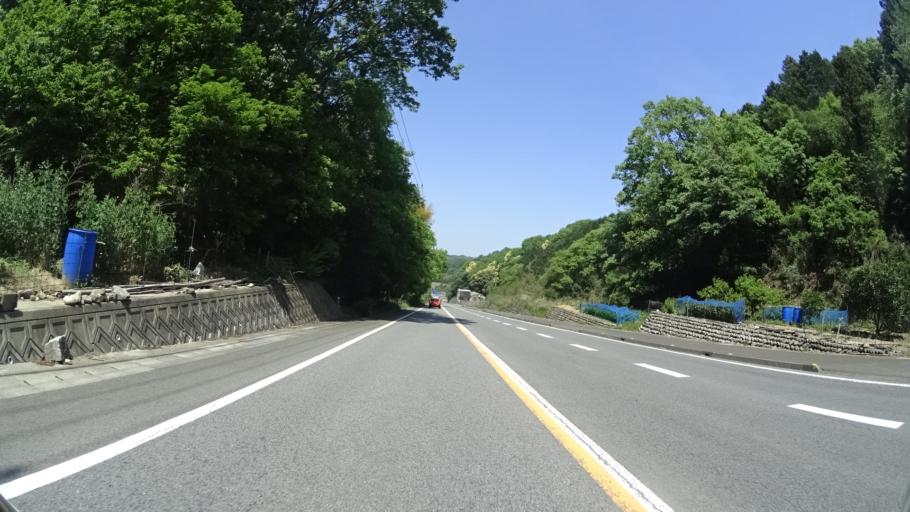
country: JP
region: Ehime
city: Hojo
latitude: 33.9983
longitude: 132.9350
